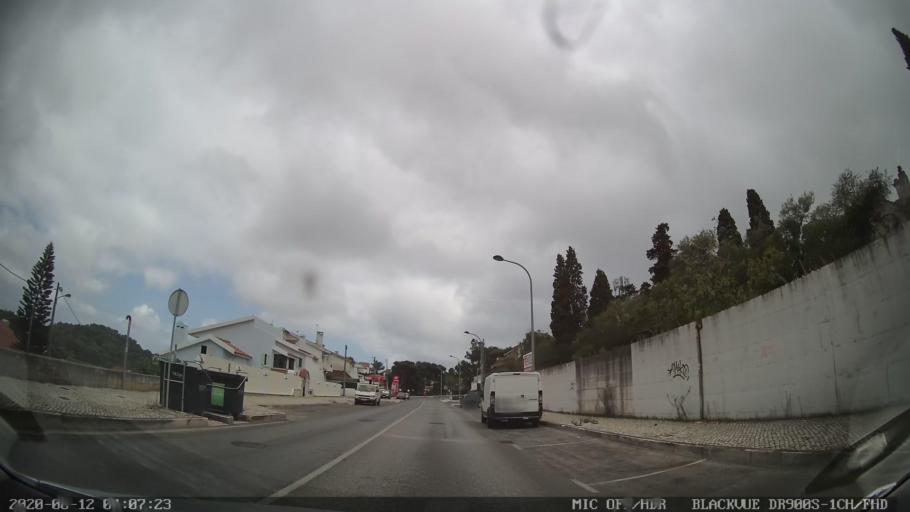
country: PT
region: Lisbon
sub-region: Cascais
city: Estoril
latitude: 38.7125
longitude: -9.3867
